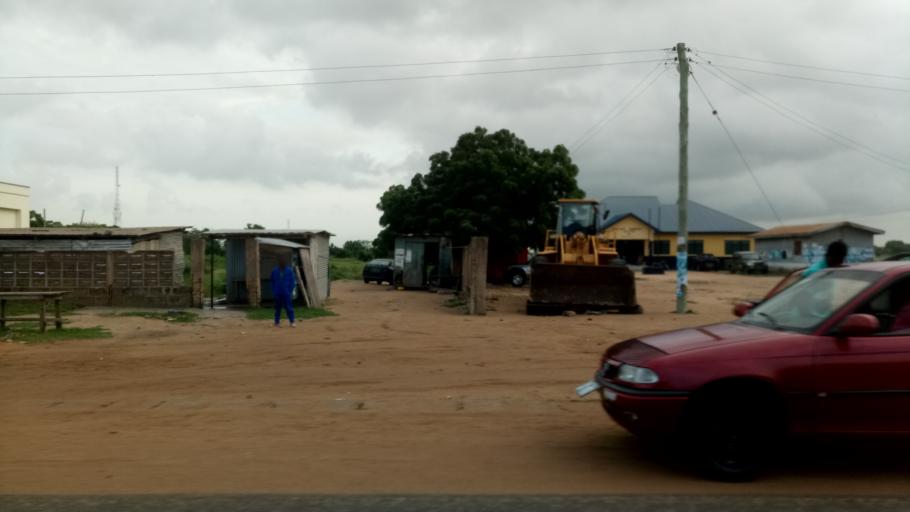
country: GH
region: Greater Accra
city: Tema
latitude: 5.8751
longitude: 0.3627
